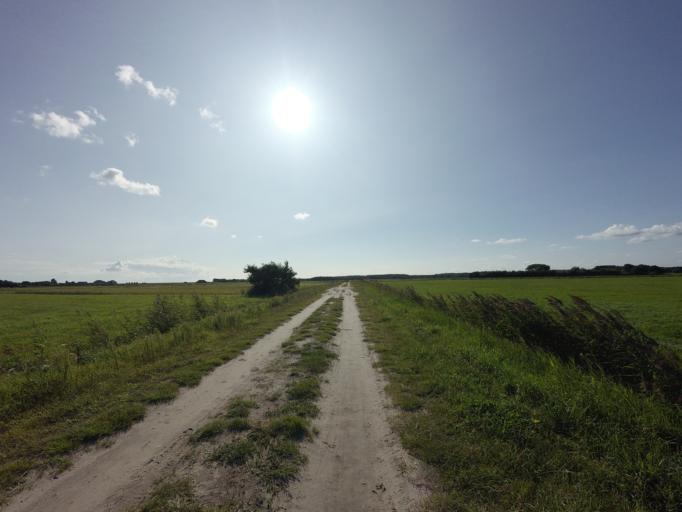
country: NL
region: Friesland
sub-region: Gemeente Terschelling
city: West-Terschelling
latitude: 53.3838
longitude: 5.2760
